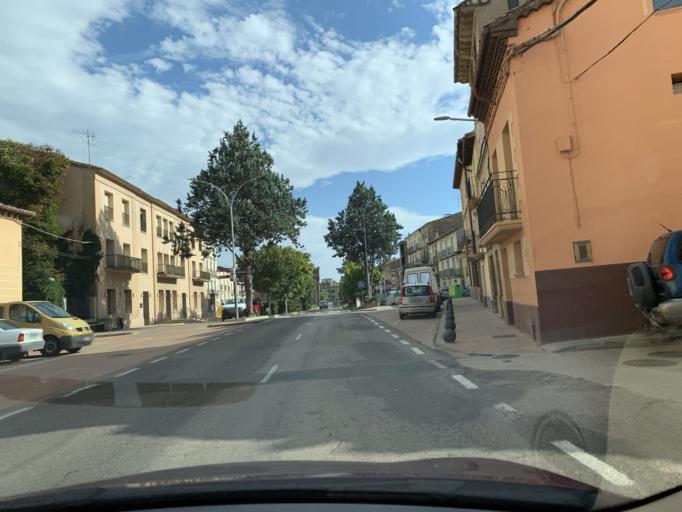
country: ES
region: Aragon
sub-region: Provincia de Huesca
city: Ayerbe
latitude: 42.2780
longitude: -0.6895
